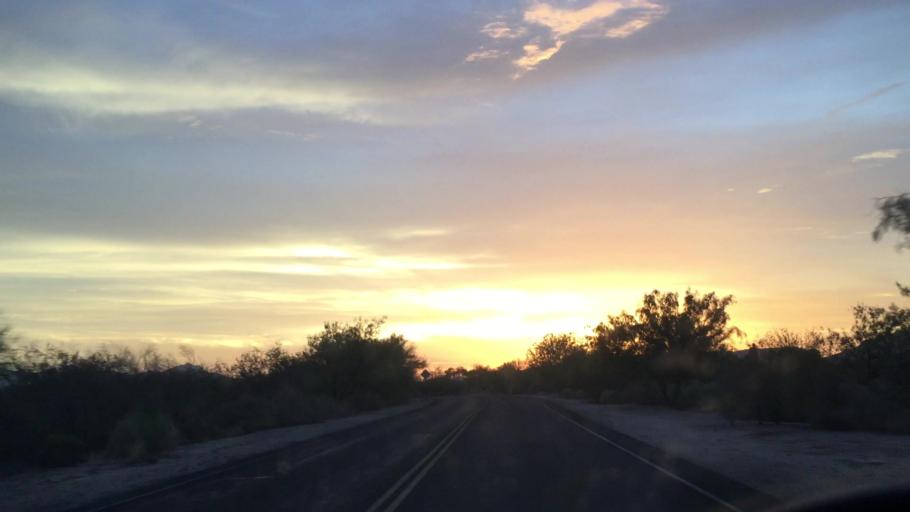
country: US
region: Arizona
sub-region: Maricopa County
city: Guadalupe
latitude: 33.2751
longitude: -111.9865
